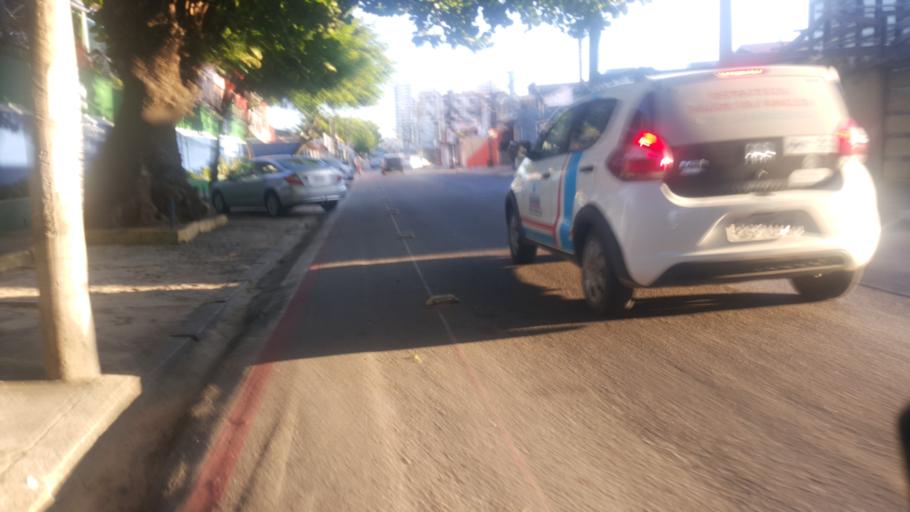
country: BR
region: Ceara
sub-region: Fortaleza
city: Fortaleza
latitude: -3.7414
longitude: -38.5340
